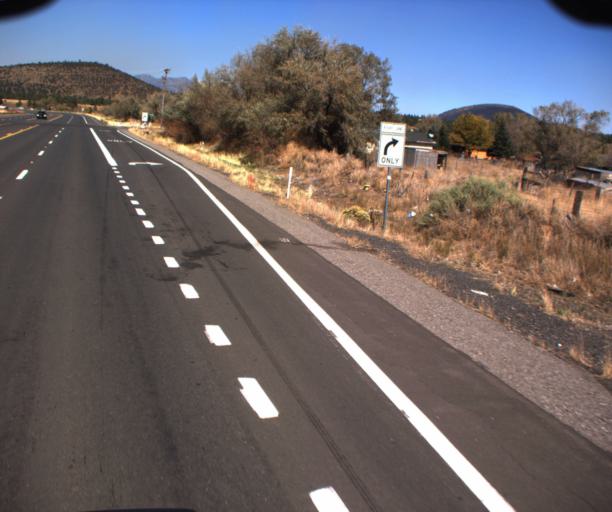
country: US
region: Arizona
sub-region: Coconino County
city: Flagstaff
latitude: 35.3203
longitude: -111.5427
